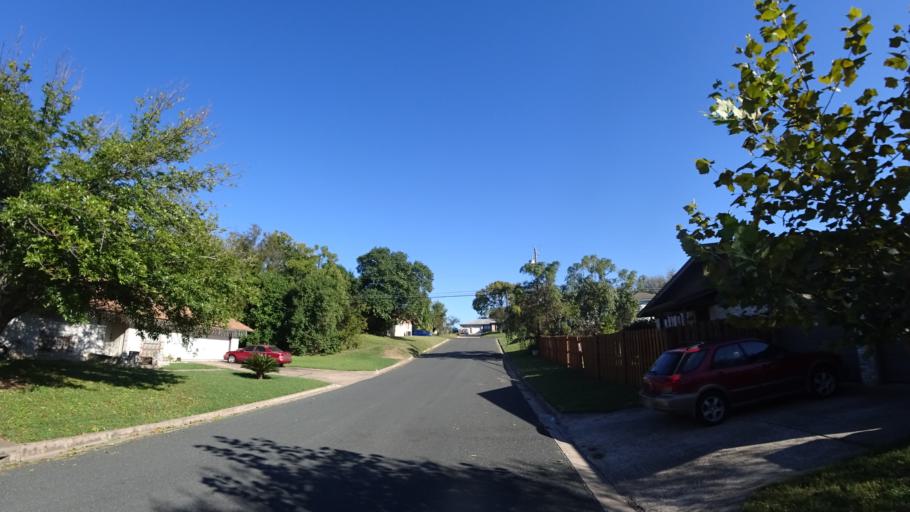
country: US
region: Texas
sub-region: Travis County
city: Austin
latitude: 30.2898
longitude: -97.6742
